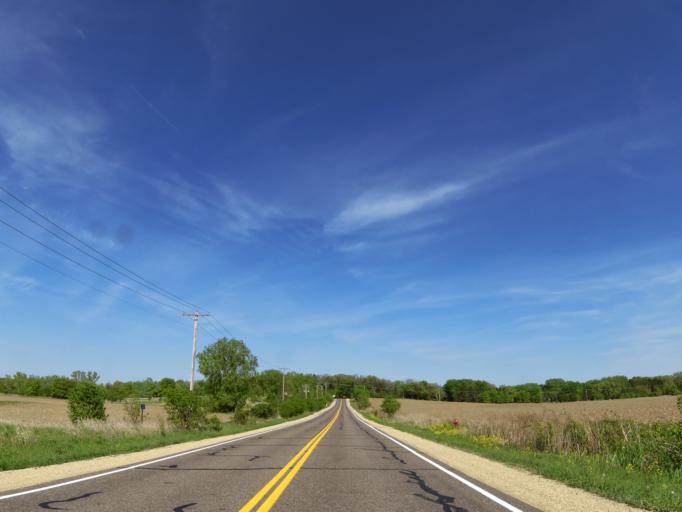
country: US
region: Minnesota
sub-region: Ramsey County
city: North Saint Paul
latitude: 45.0066
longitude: -92.9493
